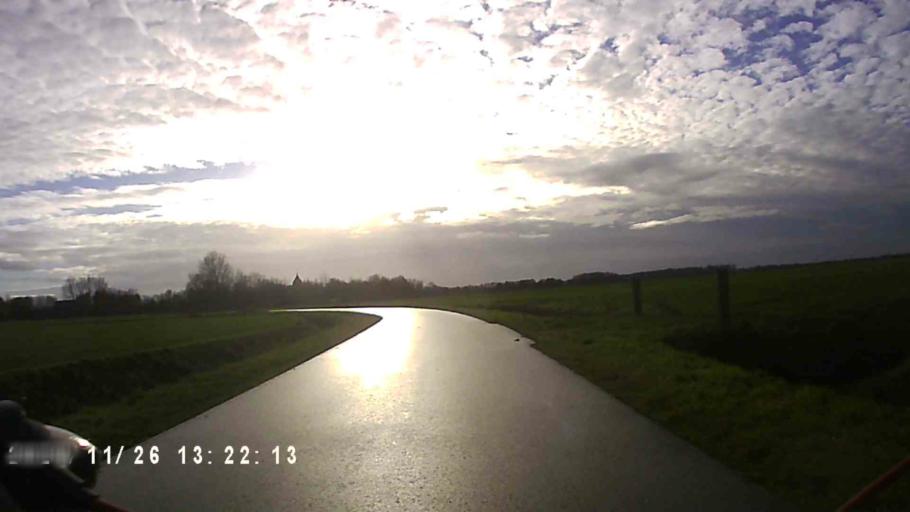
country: NL
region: Groningen
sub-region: Gemeente Delfzijl
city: Delfzijl
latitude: 53.3461
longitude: 6.8930
